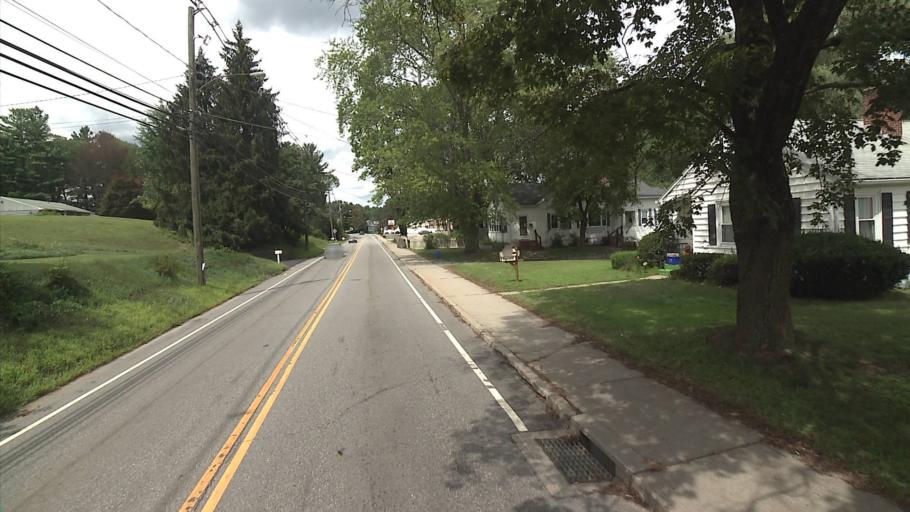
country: US
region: Connecticut
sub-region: Windham County
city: Putnam
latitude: 41.9267
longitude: -71.9208
